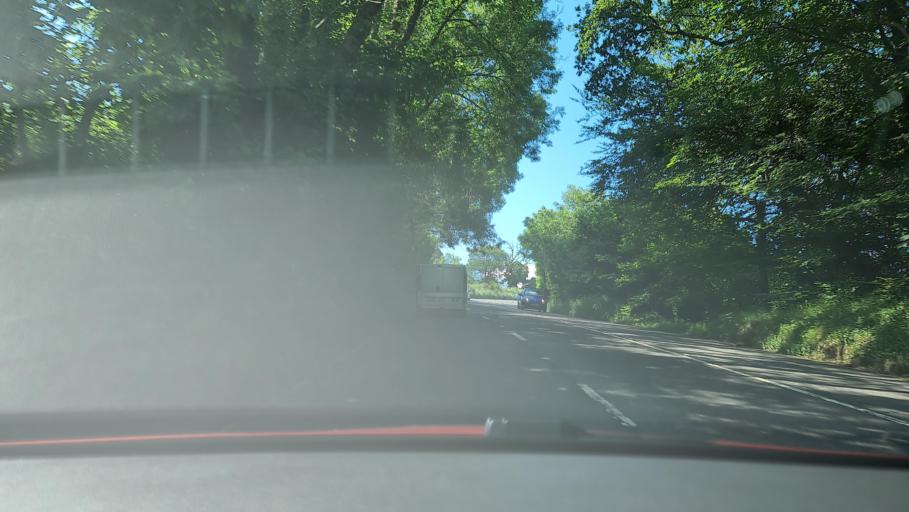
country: GB
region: England
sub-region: Cornwall
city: Lostwithiel
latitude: 50.4030
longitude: -4.6827
